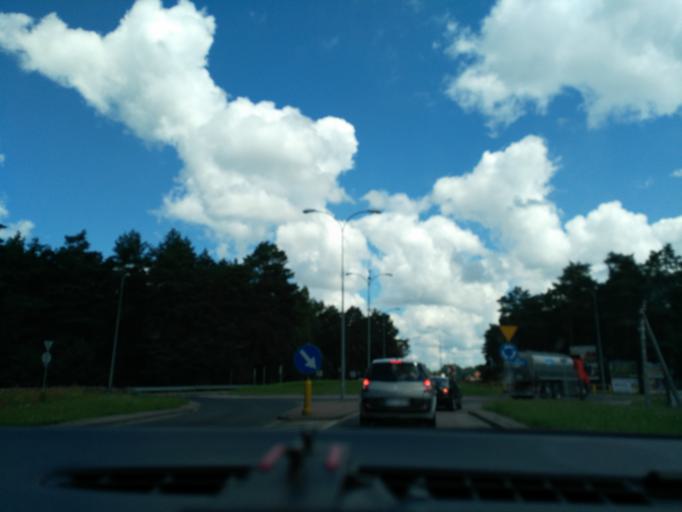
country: PL
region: Podlasie
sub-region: Powiat siemiatycki
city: Siemiatycze
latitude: 52.3932
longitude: 22.8703
